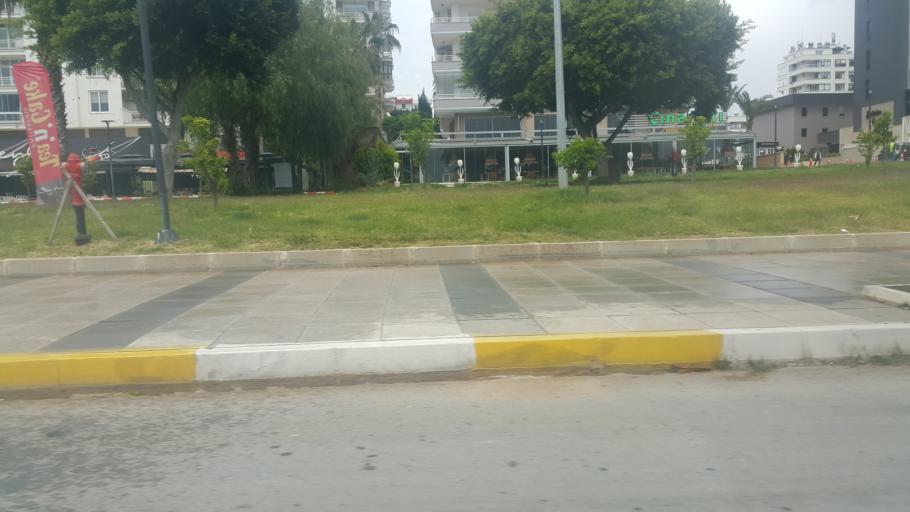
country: TR
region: Mersin
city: Mercin
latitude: 36.7698
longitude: 34.5637
